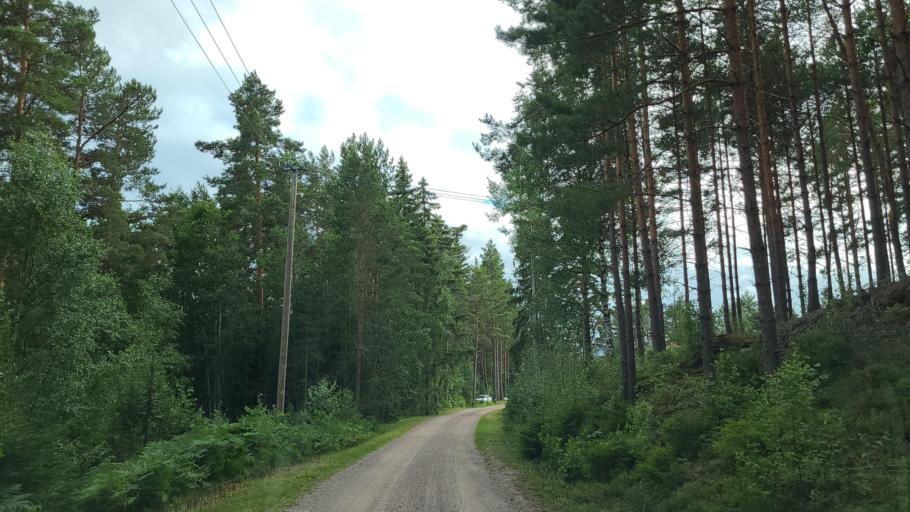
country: FI
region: Varsinais-Suomi
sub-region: Aboland-Turunmaa
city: Nagu
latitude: 60.1323
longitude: 21.7995
